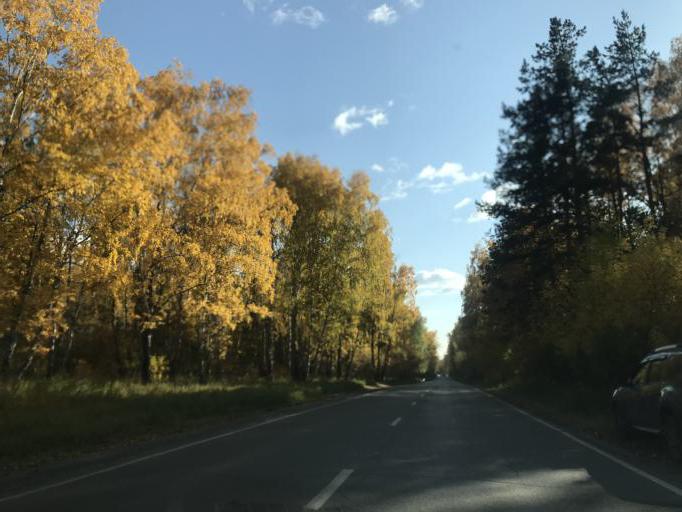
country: RU
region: Chelyabinsk
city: Dolgoderevenskoye
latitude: 55.2696
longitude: 61.3650
